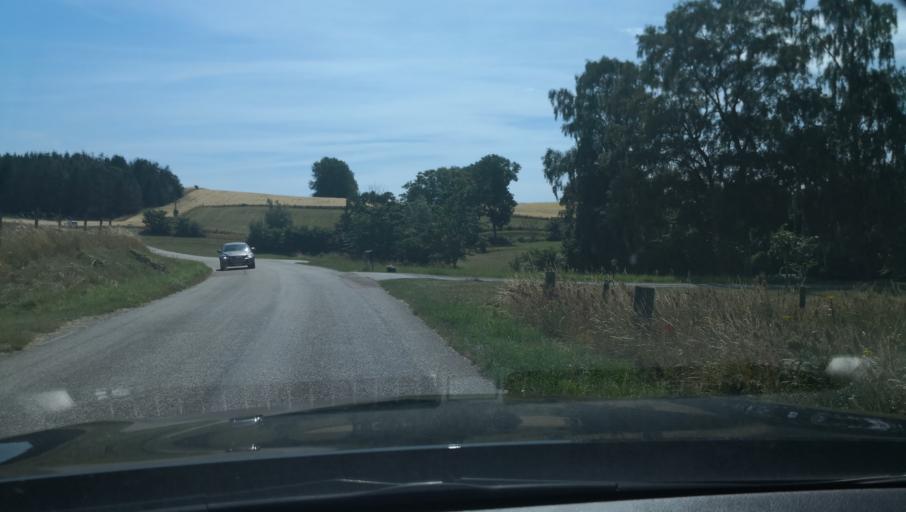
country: SE
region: Skane
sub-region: Ystads Kommun
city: Kopingebro
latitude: 55.3927
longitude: 14.1383
